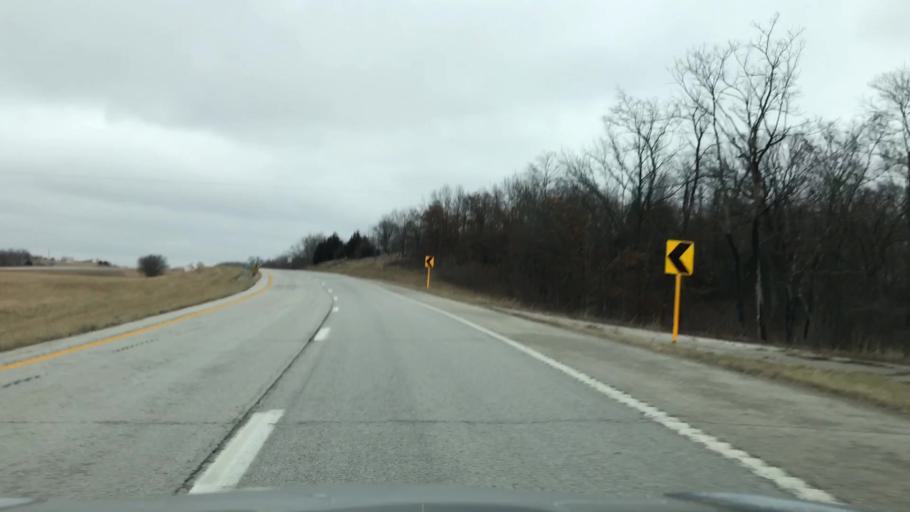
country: US
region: Missouri
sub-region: Linn County
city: Marceline
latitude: 39.7604
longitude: -92.9287
